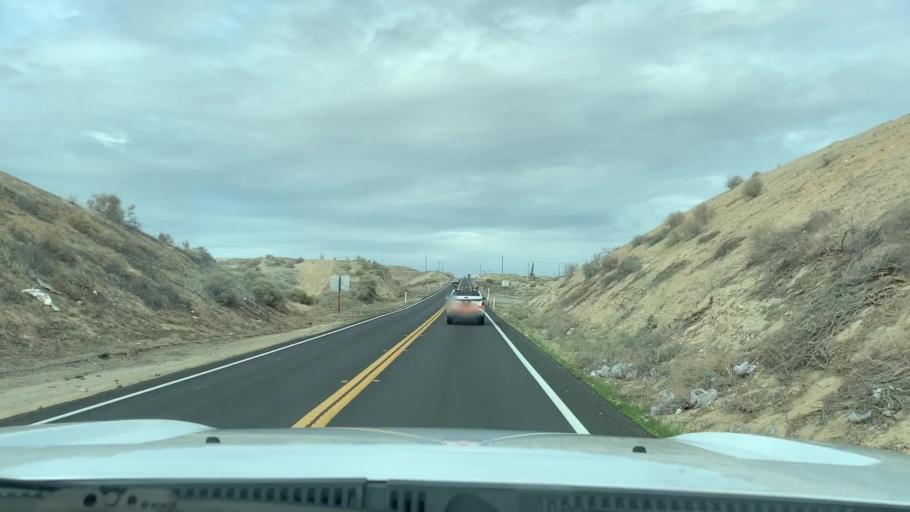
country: US
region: California
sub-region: Kern County
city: South Taft
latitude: 35.1108
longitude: -119.4253
